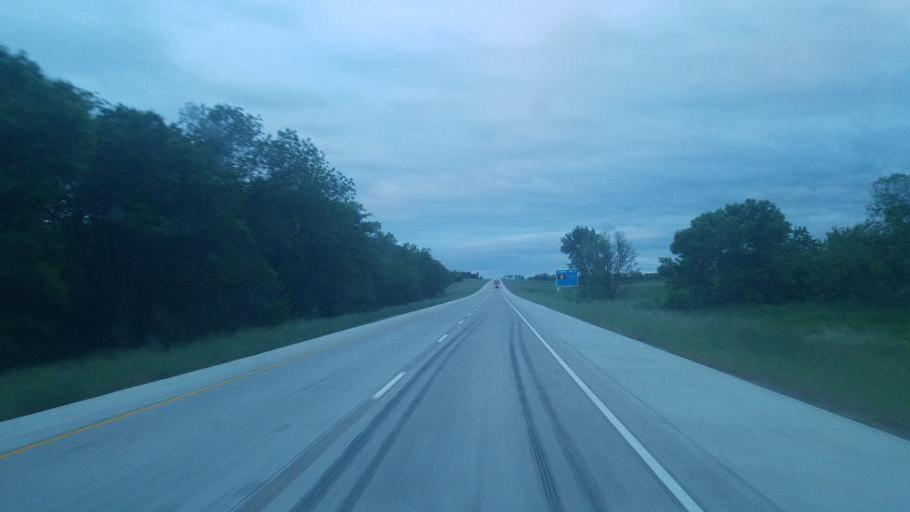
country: US
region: Iowa
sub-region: Decatur County
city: Lamoni
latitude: 40.6079
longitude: -93.9019
